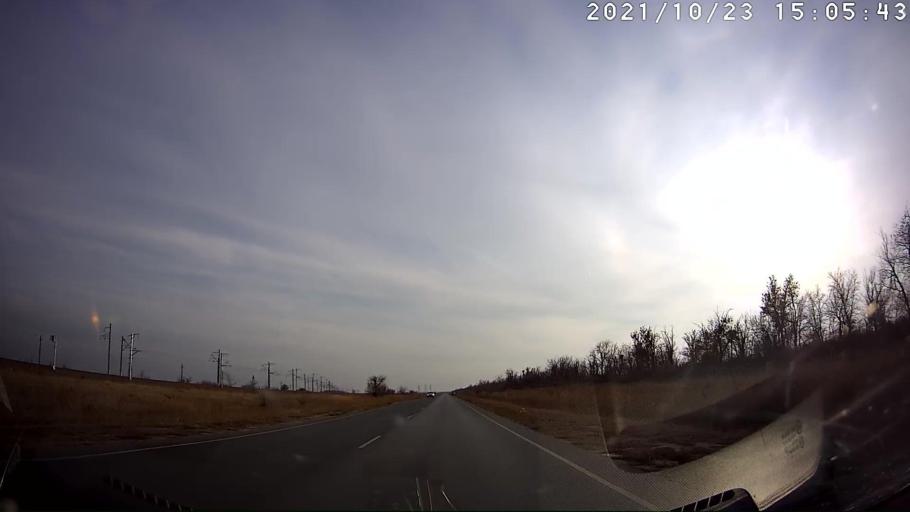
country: RU
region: Volgograd
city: Volgograd
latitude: 48.3809
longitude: 44.3592
